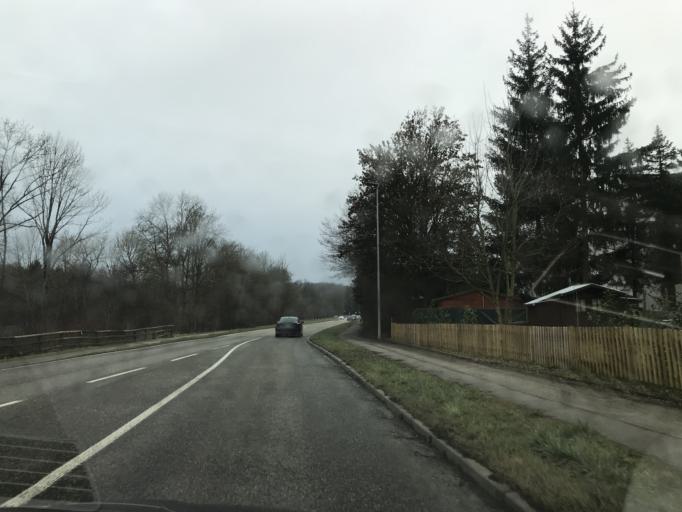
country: DE
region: Baden-Wuerttemberg
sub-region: Regierungsbezirk Stuttgart
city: Neckartailfingen
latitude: 48.6289
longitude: 9.2753
